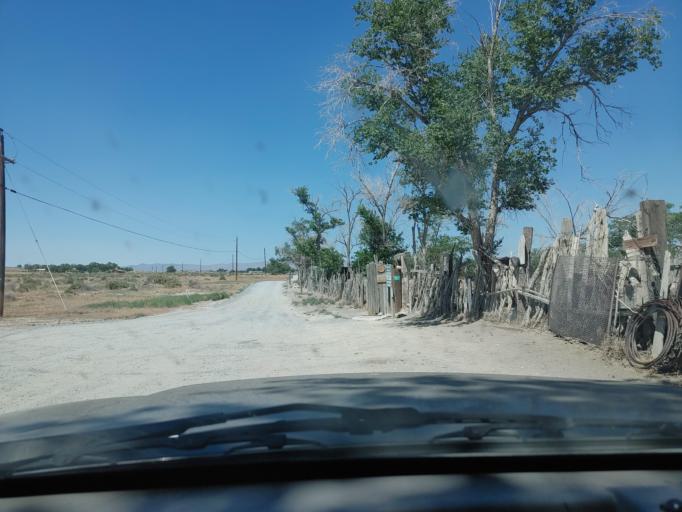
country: US
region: Nevada
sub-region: Humboldt County
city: Winnemucca
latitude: 40.6596
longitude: -118.1322
